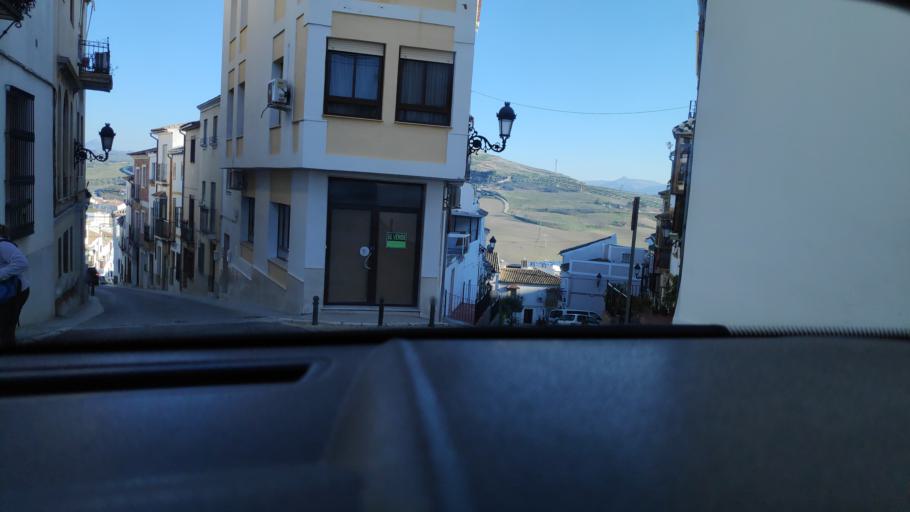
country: ES
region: Andalusia
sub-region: Province of Cordoba
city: Baena
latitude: 37.6143
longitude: -4.3253
